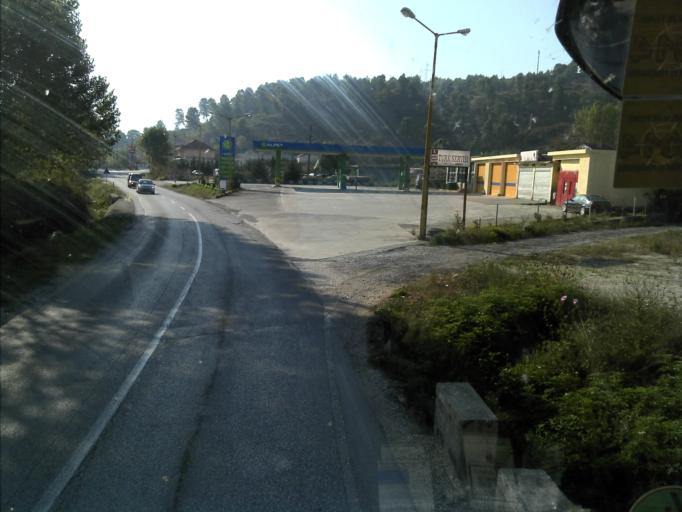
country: AL
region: Gjirokaster
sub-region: Rrethi i Gjirokastres
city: Lazarat
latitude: 40.0658
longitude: 20.1649
